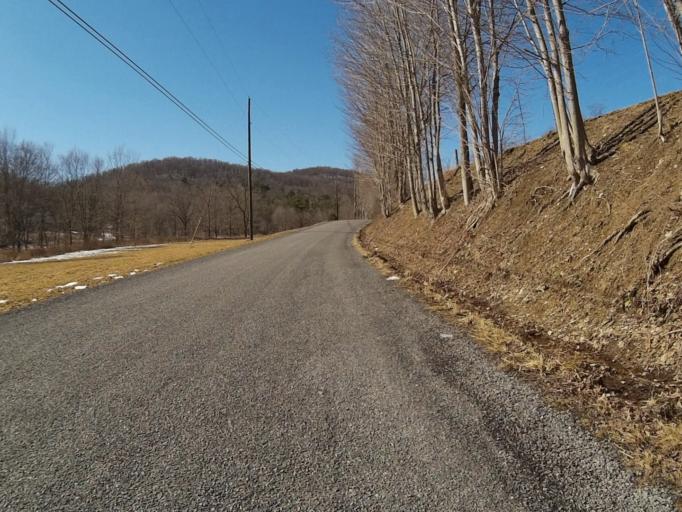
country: US
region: Pennsylvania
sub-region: Centre County
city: Stormstown
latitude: 40.8368
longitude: -78.0183
